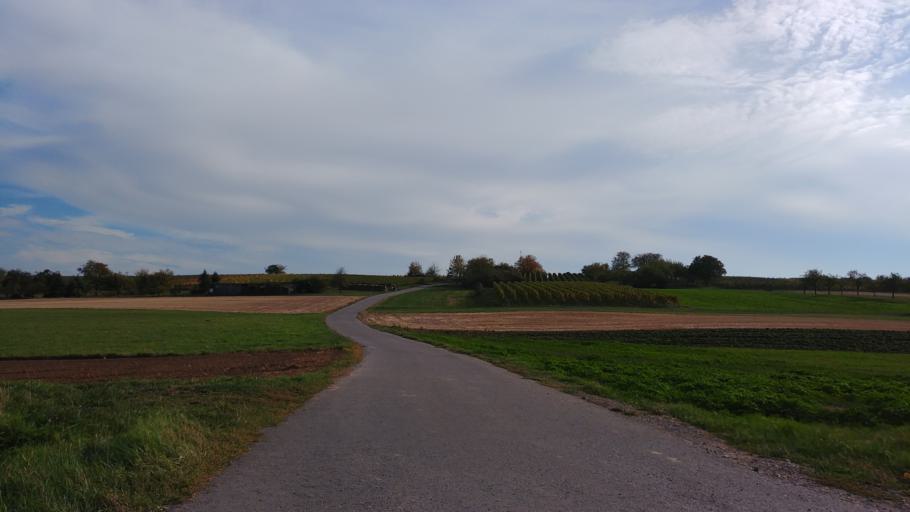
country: DE
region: Baden-Wuerttemberg
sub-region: Regierungsbezirk Stuttgart
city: Ilsfeld
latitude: 49.0722
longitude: 9.2438
